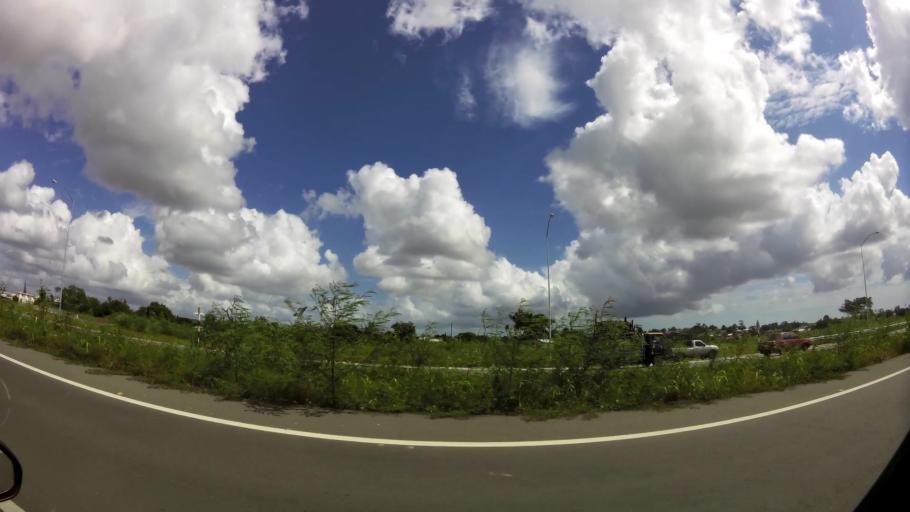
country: TT
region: Penal/Debe
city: Debe
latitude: 10.2140
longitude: -61.4572
